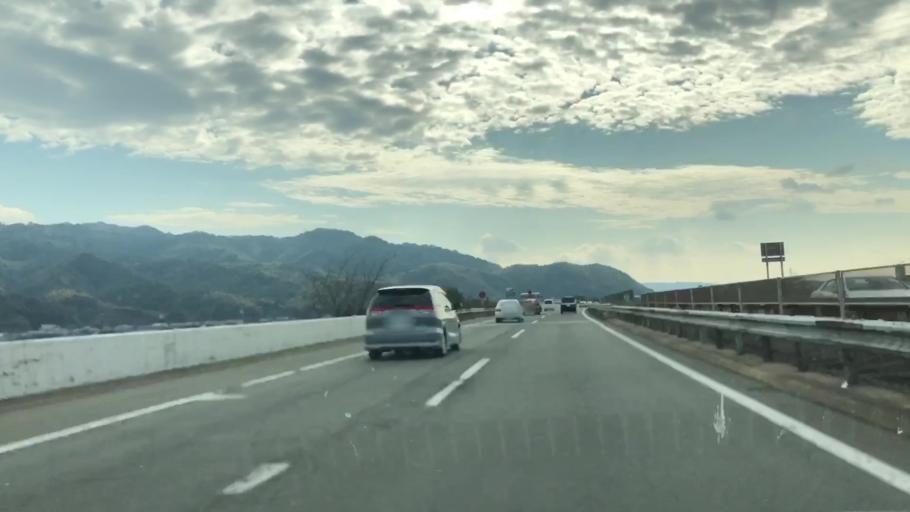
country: JP
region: Fukuoka
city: Setakamachi-takayanagi
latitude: 33.1805
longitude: 130.5179
